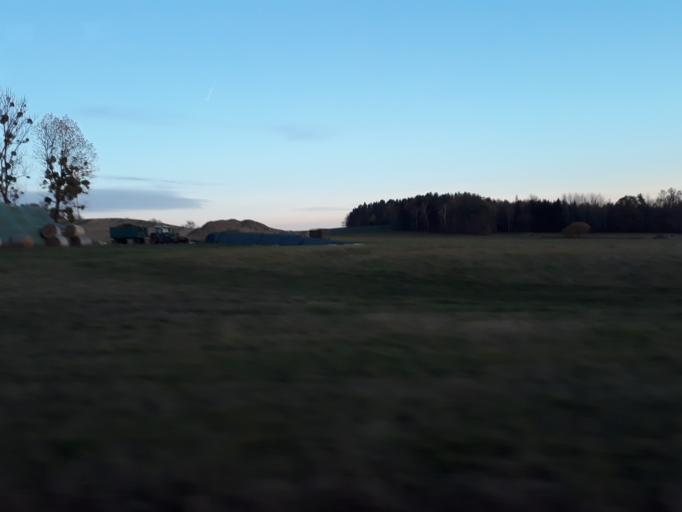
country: DE
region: Saxony
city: Reinhardtsgrimma
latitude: 50.9010
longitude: 13.7839
